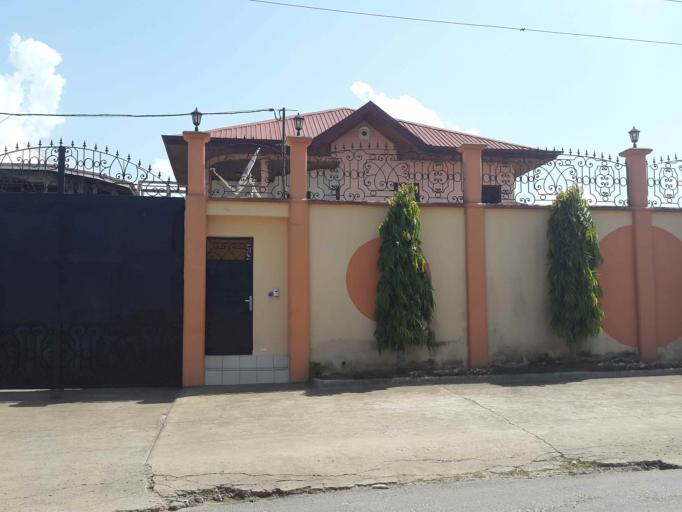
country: CM
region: Littoral
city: Douala
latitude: 4.0939
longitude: 9.7355
